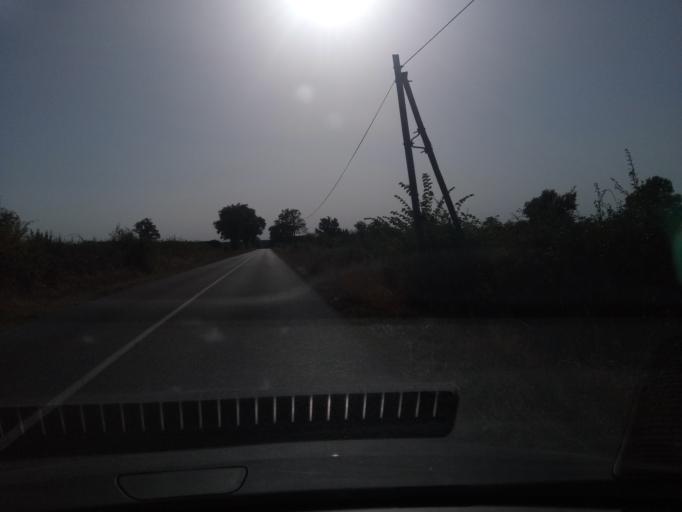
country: FR
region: Poitou-Charentes
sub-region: Departement de la Vienne
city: Lathus-Saint-Remy
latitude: 46.4588
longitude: 1.0273
